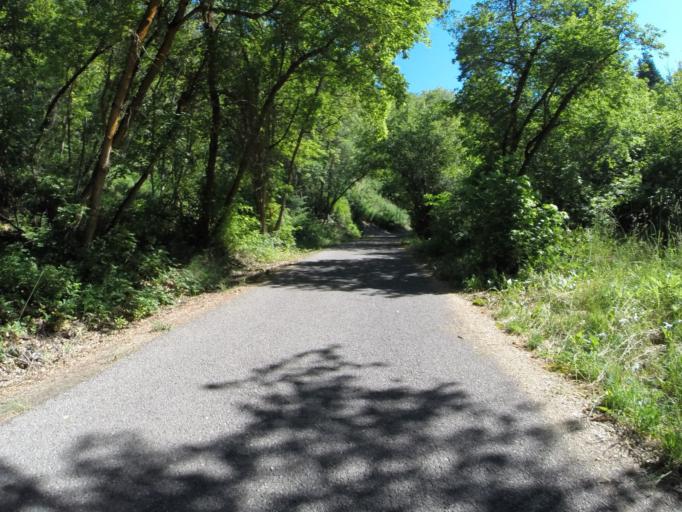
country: US
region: Utah
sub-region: Davis County
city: Woods Cross
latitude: 40.8189
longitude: -111.8173
